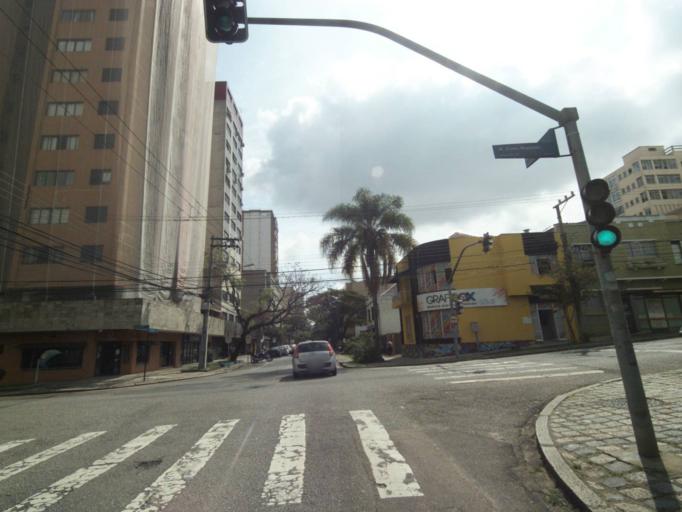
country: BR
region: Parana
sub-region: Curitiba
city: Curitiba
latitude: -25.4302
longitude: -49.2607
